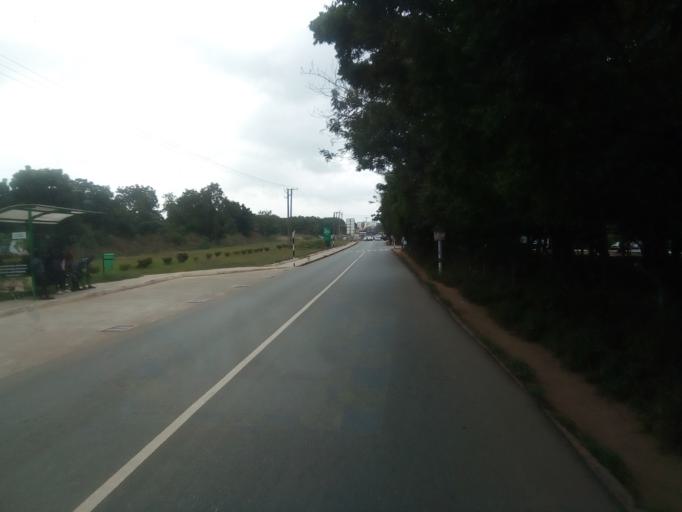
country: GH
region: Greater Accra
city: Dome
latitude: 5.6397
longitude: -0.2079
